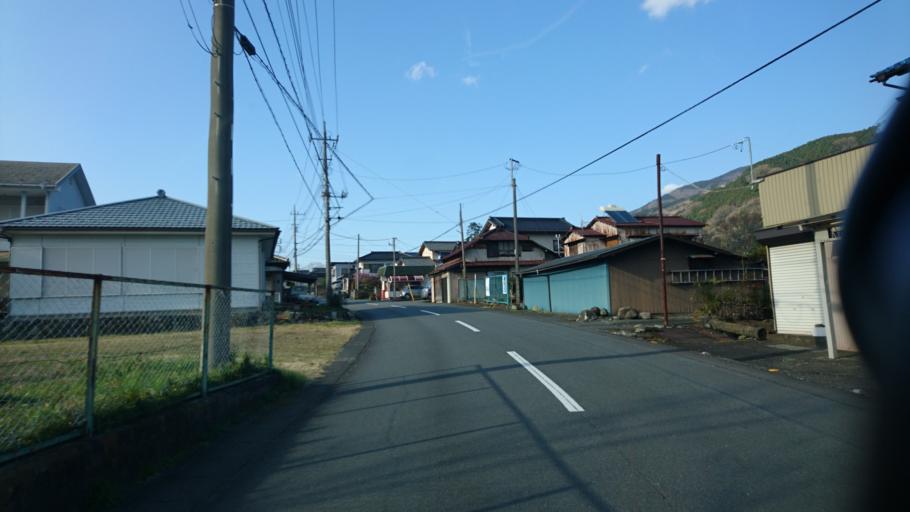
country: JP
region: Shizuoka
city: Fujinomiya
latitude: 35.3044
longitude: 138.4501
